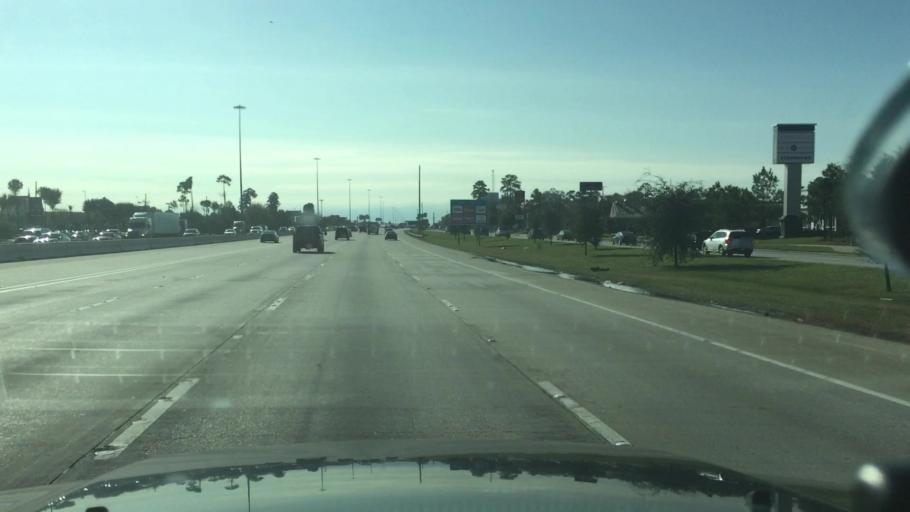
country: US
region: Texas
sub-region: Montgomery County
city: Shenandoah
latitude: 30.1900
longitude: -95.4533
